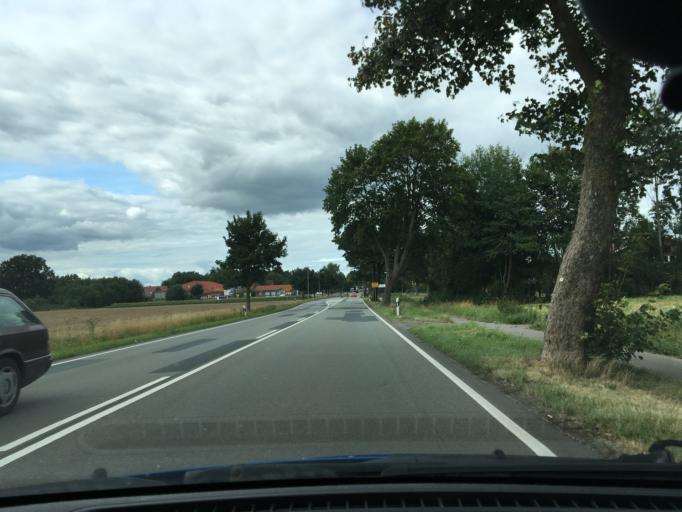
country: DE
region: Lower Saxony
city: Neu Wulmstorf
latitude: 53.4199
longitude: 9.7896
